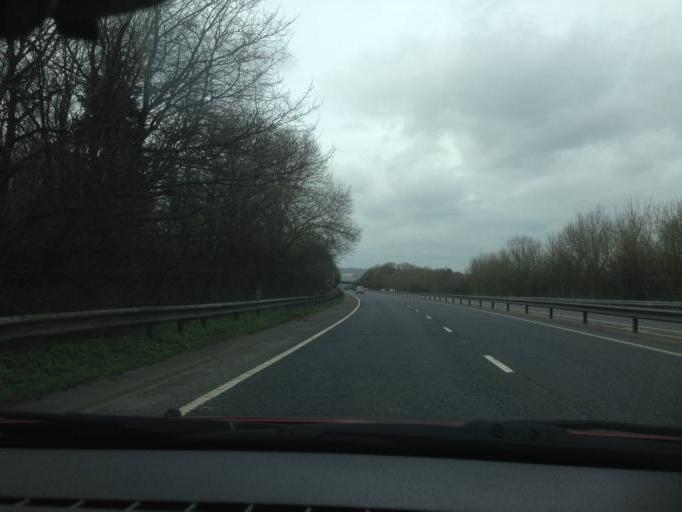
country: GB
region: England
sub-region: Kent
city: Sevenoaks
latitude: 51.2664
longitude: 0.1688
